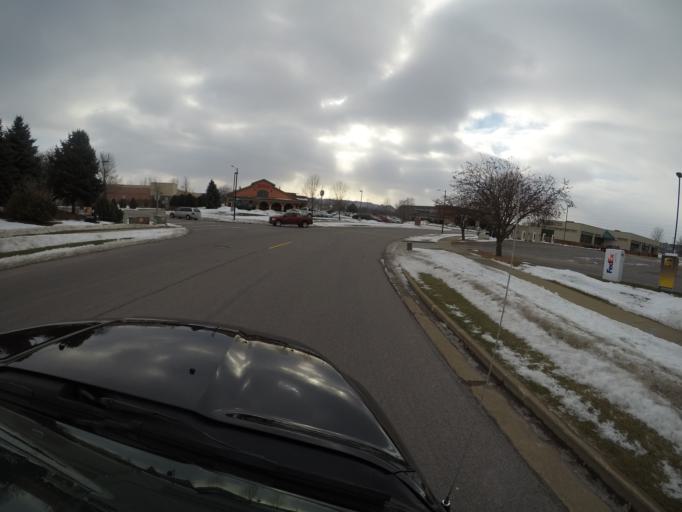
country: US
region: Wisconsin
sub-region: La Crosse County
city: Onalaska
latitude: 43.8793
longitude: -91.1877
